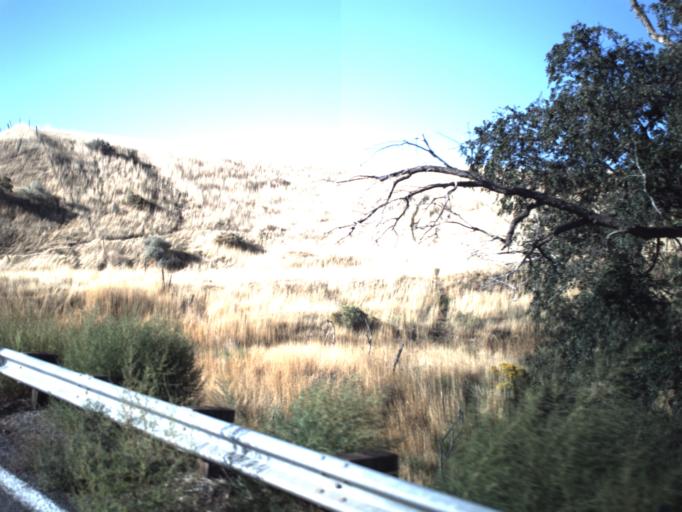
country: US
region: Utah
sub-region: Millard County
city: Delta
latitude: 39.5278
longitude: -112.2734
